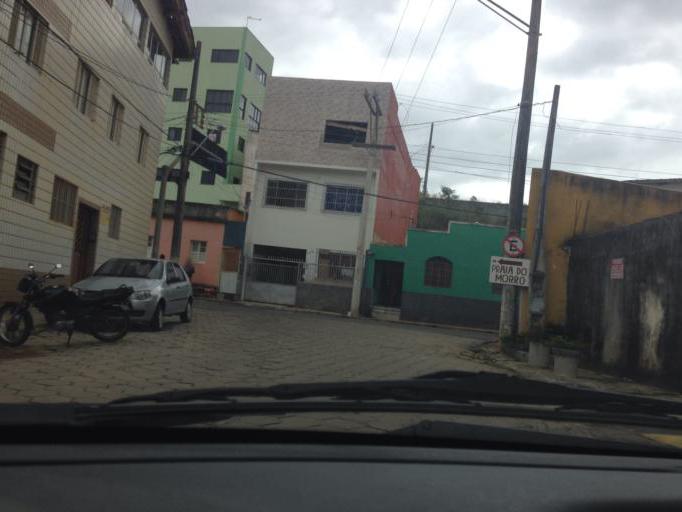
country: BR
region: Espirito Santo
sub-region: Guarapari
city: Guarapari
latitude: -20.6673
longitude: -40.4946
